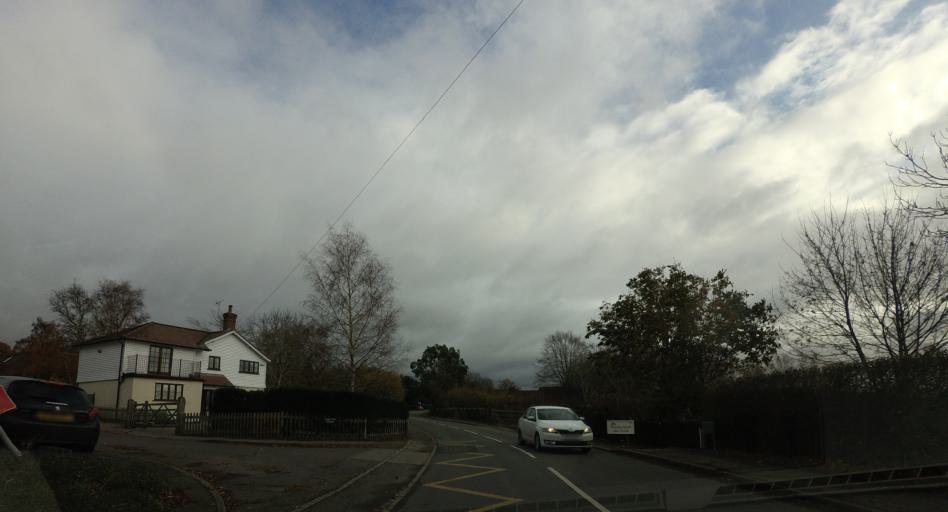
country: GB
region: England
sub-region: Kent
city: Paddock Wood
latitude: 51.1515
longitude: 0.3925
